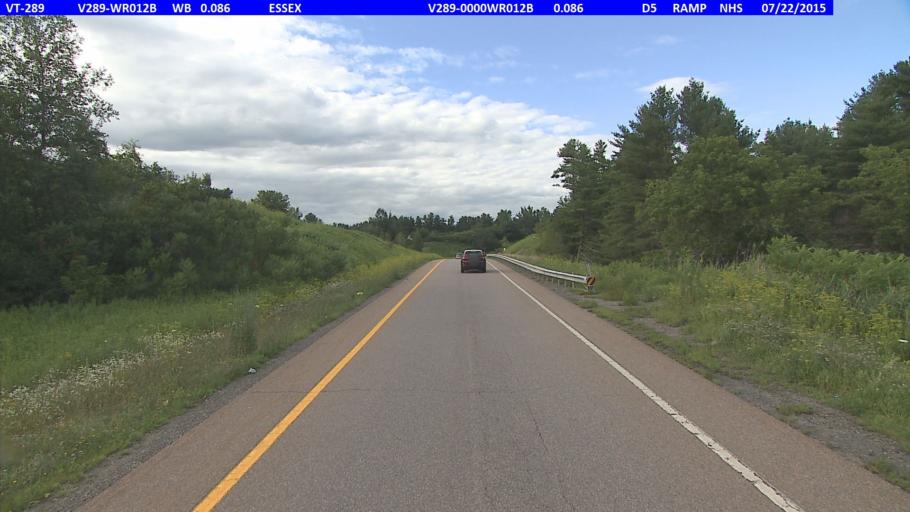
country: US
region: Vermont
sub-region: Chittenden County
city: Williston
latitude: 44.4813
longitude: -73.0674
